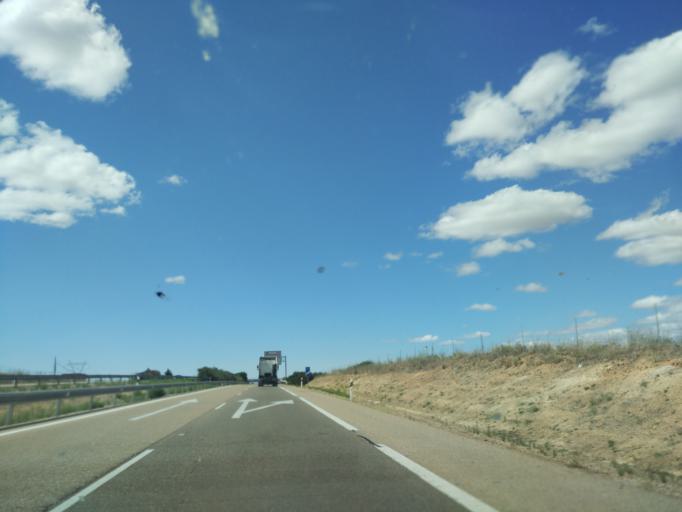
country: ES
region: Castille and Leon
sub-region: Provincia de Valladolid
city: Rueda
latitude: 41.4385
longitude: -4.9746
